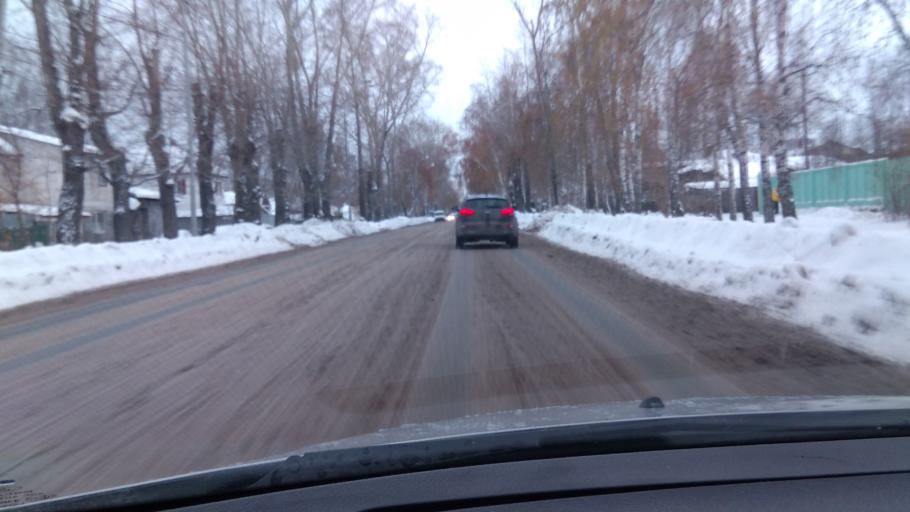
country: RU
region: Sverdlovsk
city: Yekaterinburg
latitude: 56.8105
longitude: 60.5812
